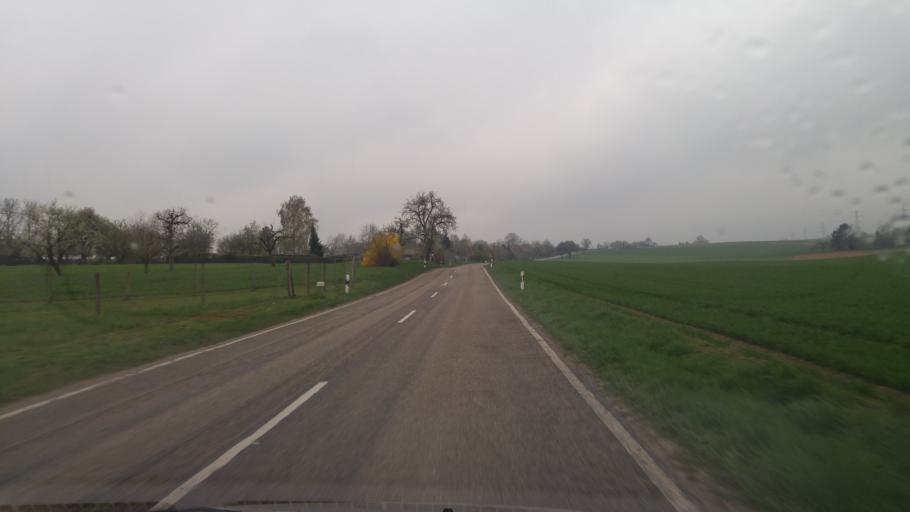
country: DE
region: Baden-Wuerttemberg
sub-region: Regierungsbezirk Stuttgart
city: Leonberg
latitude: 48.8317
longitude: 9.0275
